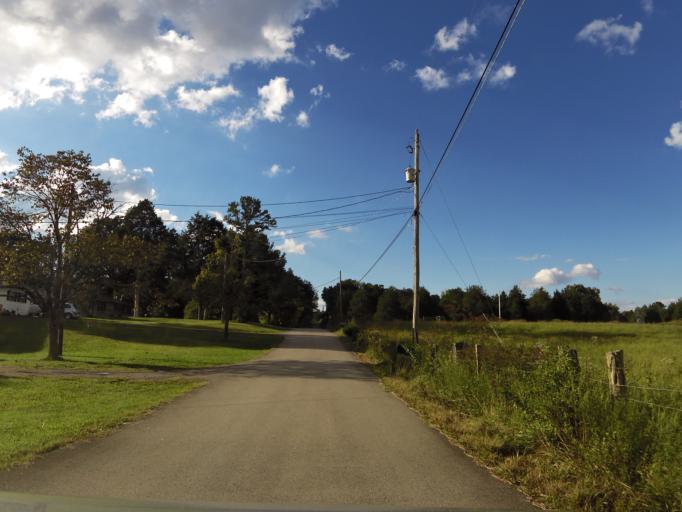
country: US
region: Tennessee
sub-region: Union County
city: Condon
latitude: 36.1288
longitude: -83.7790
